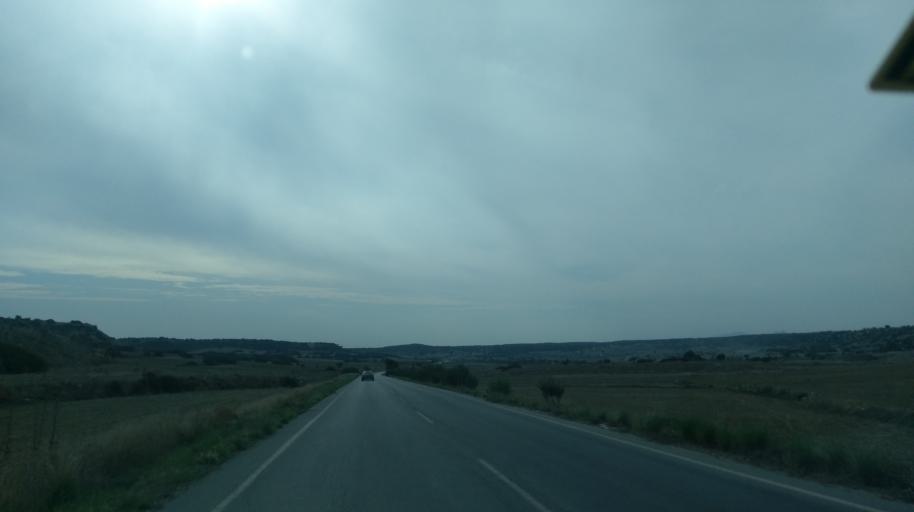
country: CY
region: Ammochostos
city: Leonarisso
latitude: 35.4657
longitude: 34.1404
